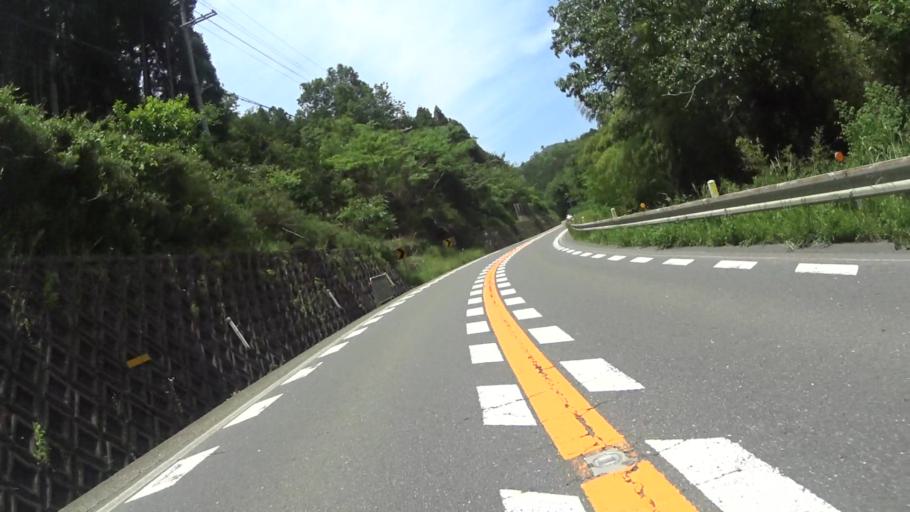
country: JP
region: Kyoto
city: Ayabe
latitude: 35.1974
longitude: 135.2833
